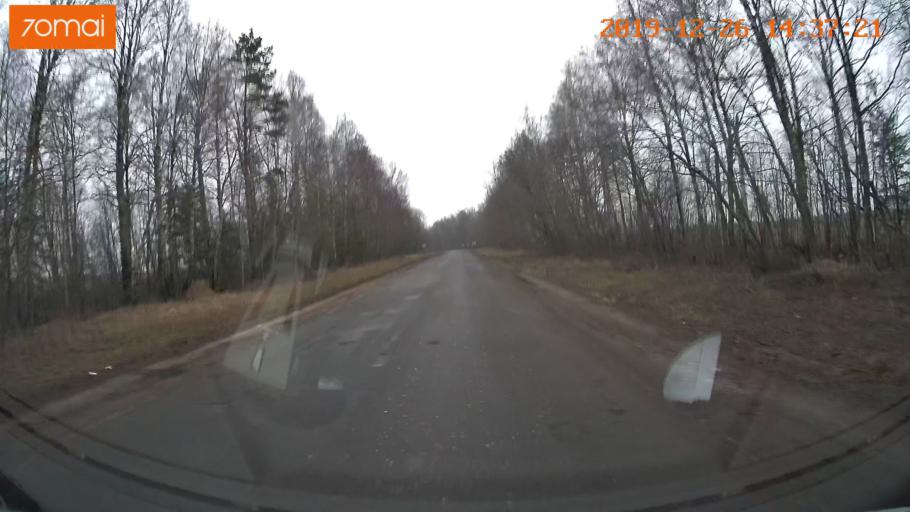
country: RU
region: Jaroslavl
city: Poshekhon'ye
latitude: 58.4031
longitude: 38.9726
